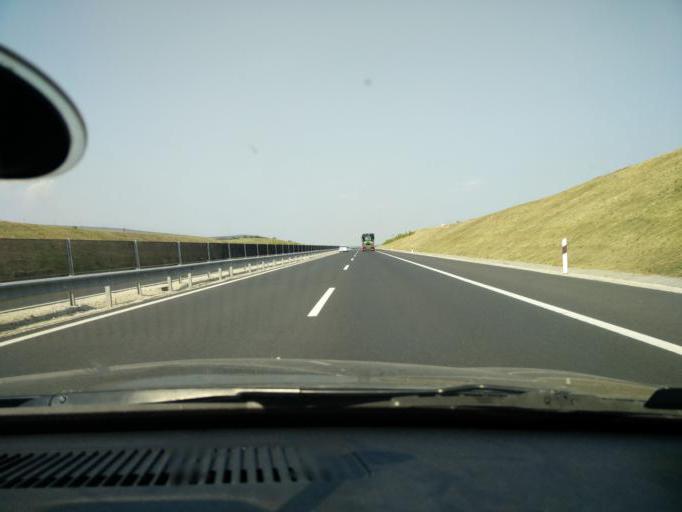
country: HU
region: Tolna
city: Szedres
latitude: 46.4796
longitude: 18.7364
